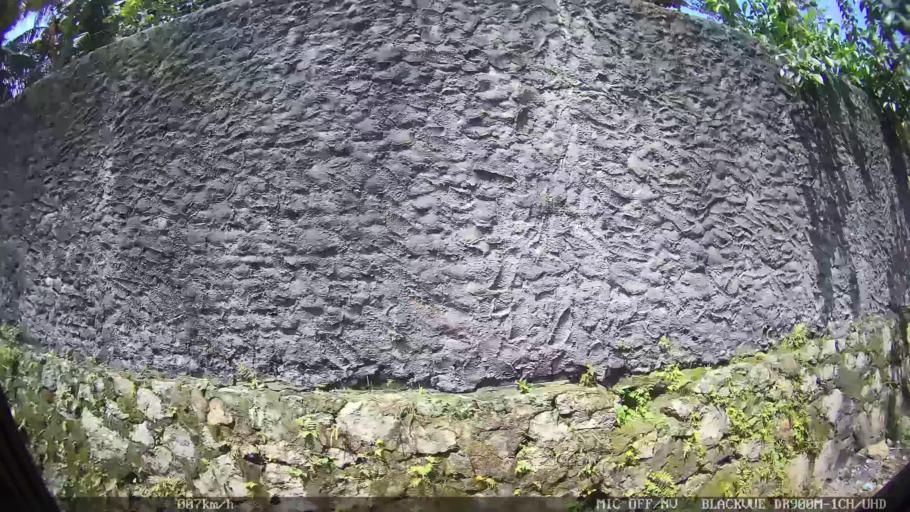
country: ID
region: Lampung
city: Kedaton
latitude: -5.3610
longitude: 105.2548
